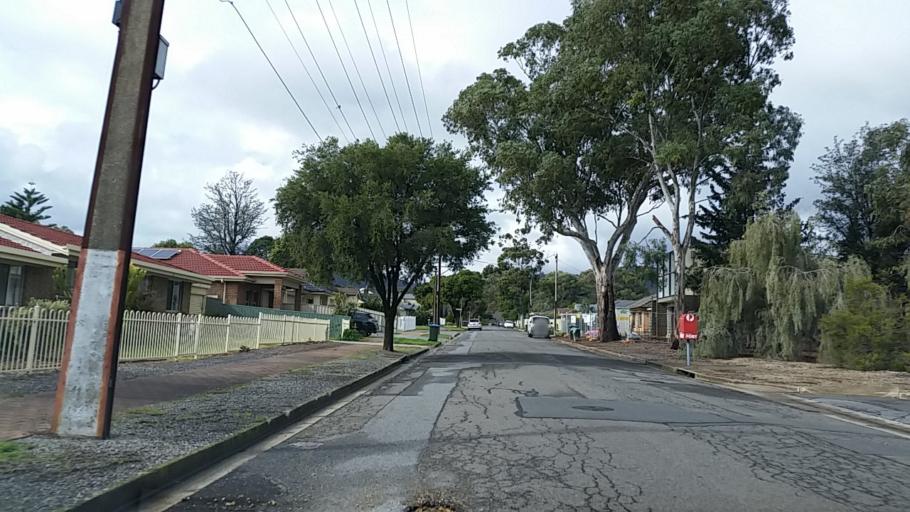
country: AU
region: South Australia
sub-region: Campbelltown
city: Campbelltown
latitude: -34.8922
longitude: 138.6764
